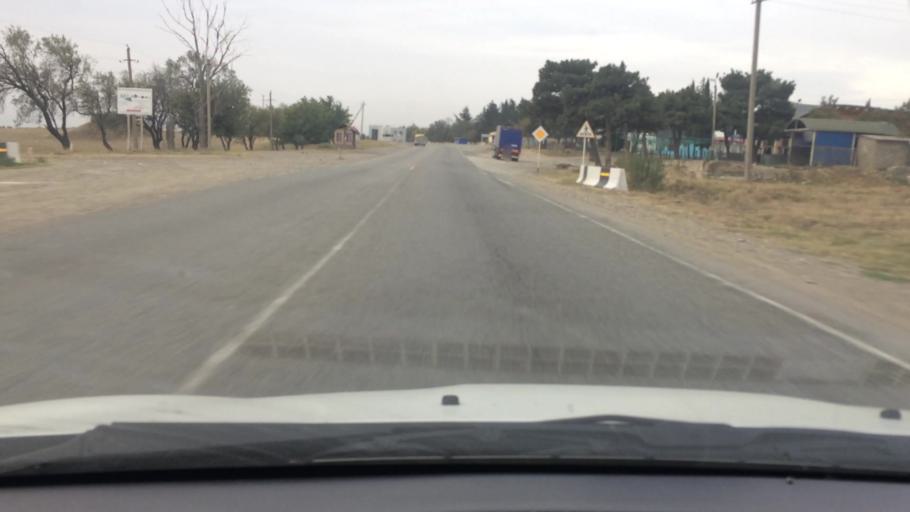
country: GE
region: T'bilisi
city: Tbilisi
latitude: 41.6303
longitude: 44.8101
